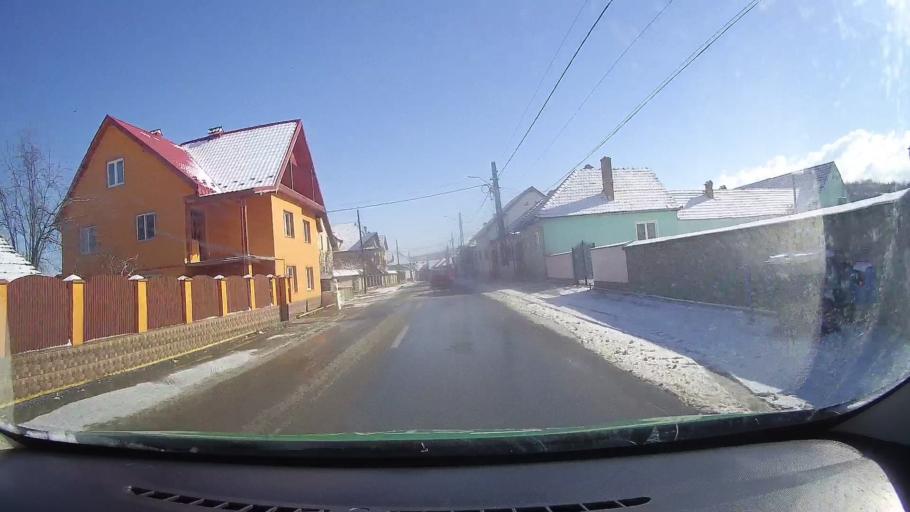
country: RO
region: Sibiu
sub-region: Comuna Racovita
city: Racovita
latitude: 45.6777
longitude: 24.3359
